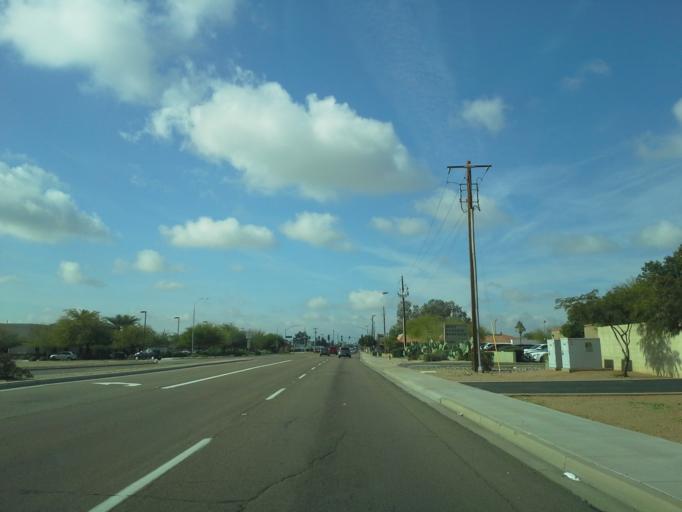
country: US
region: Arizona
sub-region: Maricopa County
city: Sun City
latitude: 33.5807
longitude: -112.2609
